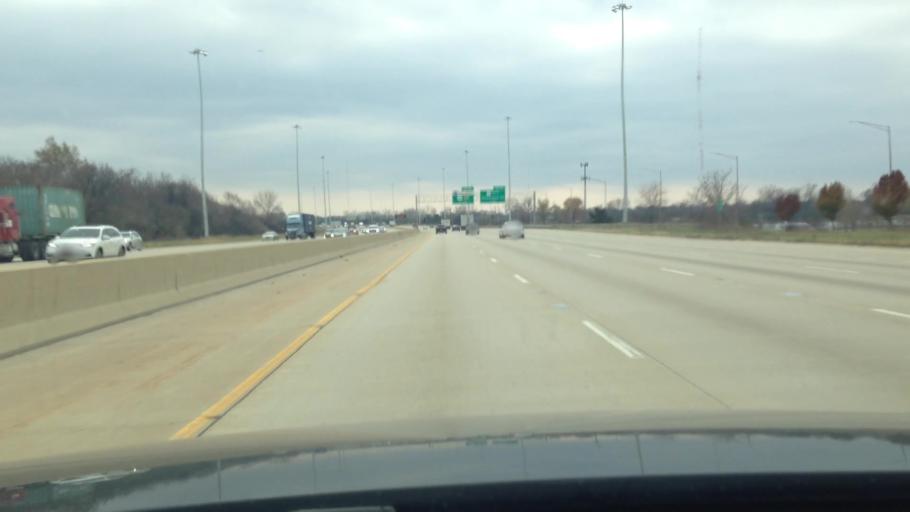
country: US
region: Illinois
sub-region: Cook County
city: Hoffman Estates
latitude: 42.0228
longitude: -88.0312
